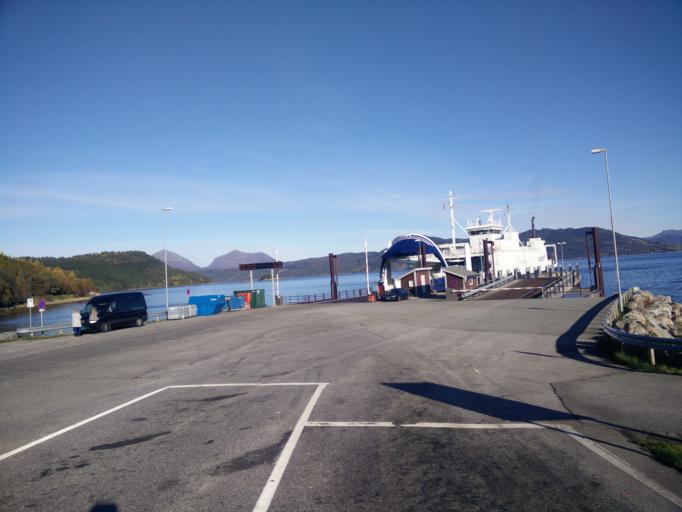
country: NO
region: More og Romsdal
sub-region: Tingvoll
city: Tingvoll
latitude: 63.0528
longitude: 8.1242
